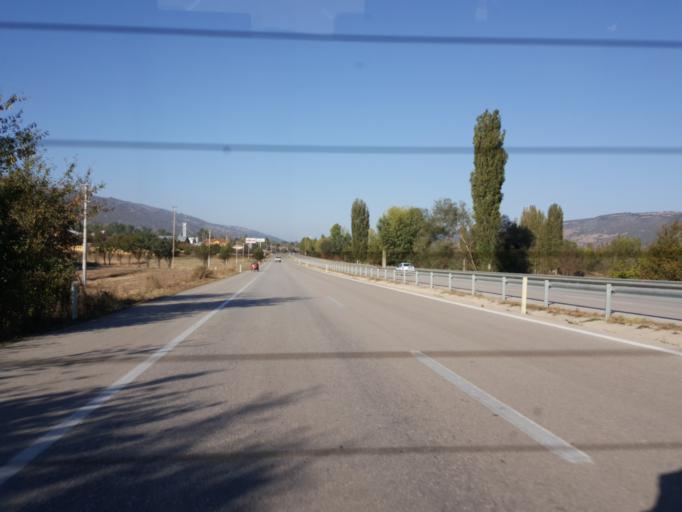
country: TR
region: Amasya
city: Ezinepazari
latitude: 40.5683
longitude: 36.0726
